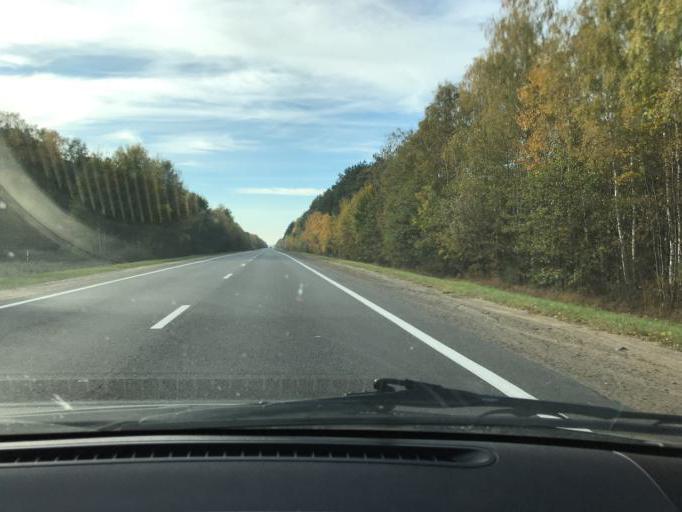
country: BY
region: Brest
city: Ivanava
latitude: 52.1572
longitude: 25.7552
